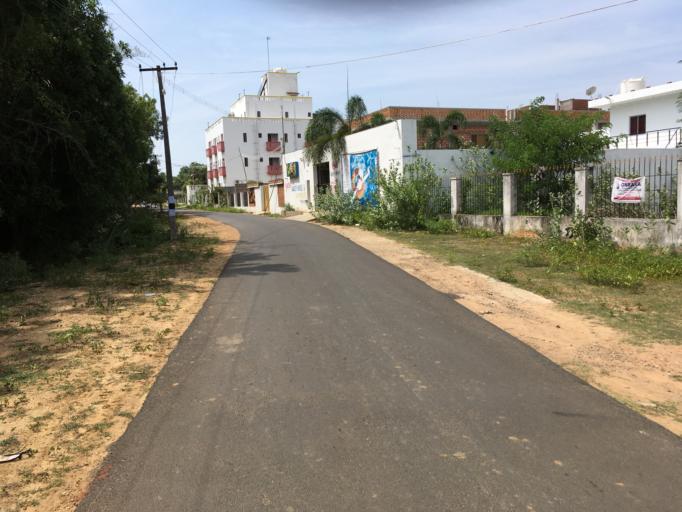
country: IN
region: Tamil Nadu
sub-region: Villupuram
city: Auroville
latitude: 12.0054
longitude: 79.7972
